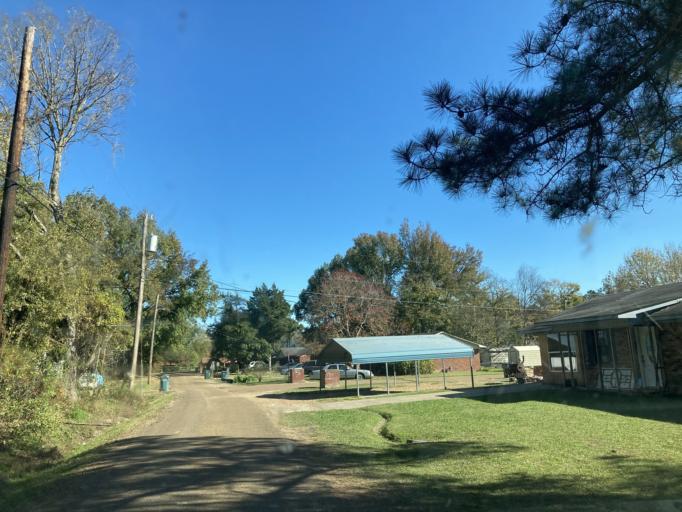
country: US
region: Mississippi
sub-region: Yazoo County
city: Yazoo City
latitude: 32.8434
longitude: -90.4291
